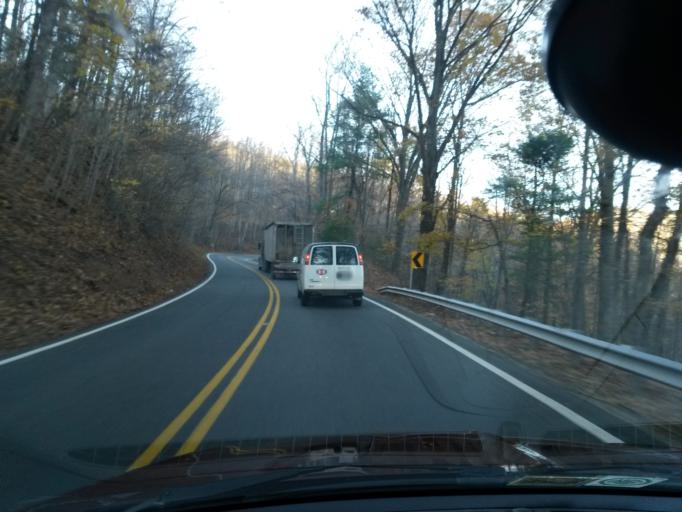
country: US
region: Virginia
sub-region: City of Buena Vista
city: Buena Vista
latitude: 37.7055
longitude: -79.2475
